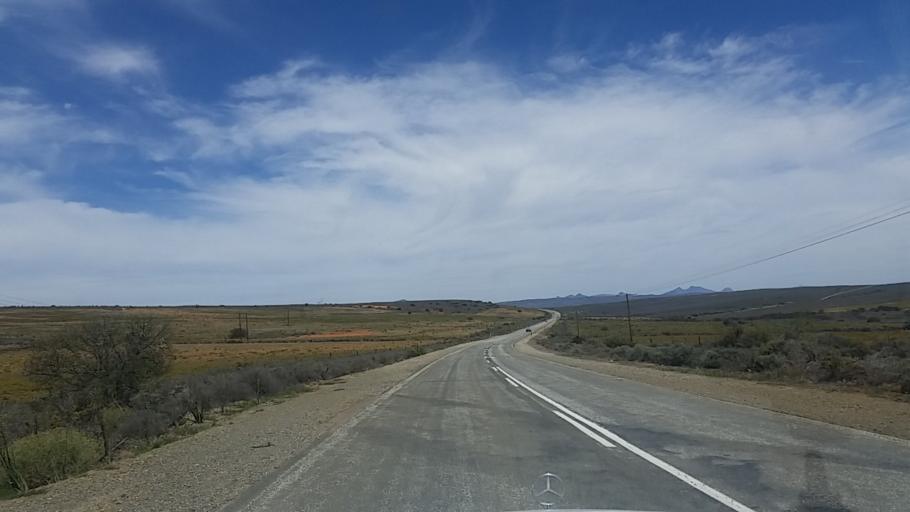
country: ZA
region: Western Cape
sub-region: Eden District Municipality
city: Knysna
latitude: -33.6209
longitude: 23.1390
